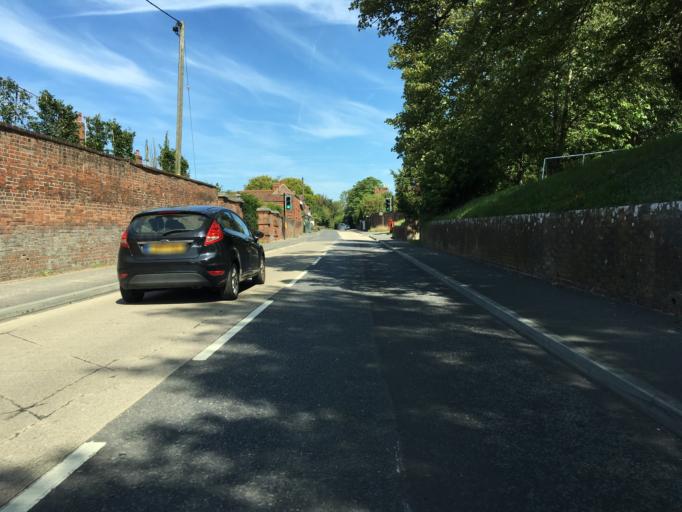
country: GB
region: England
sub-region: Hampshire
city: Compton
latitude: 51.0225
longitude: -1.3128
